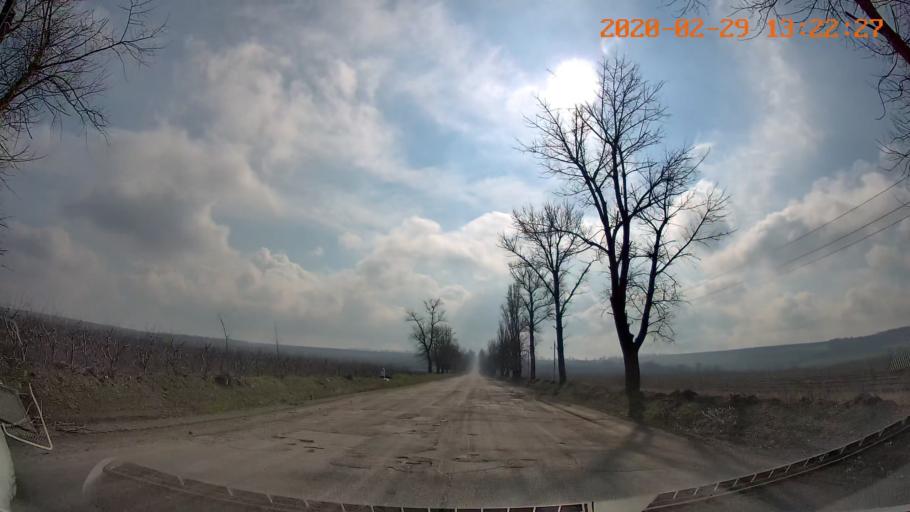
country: MD
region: Telenesti
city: Camenca
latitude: 47.9604
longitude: 28.6279
